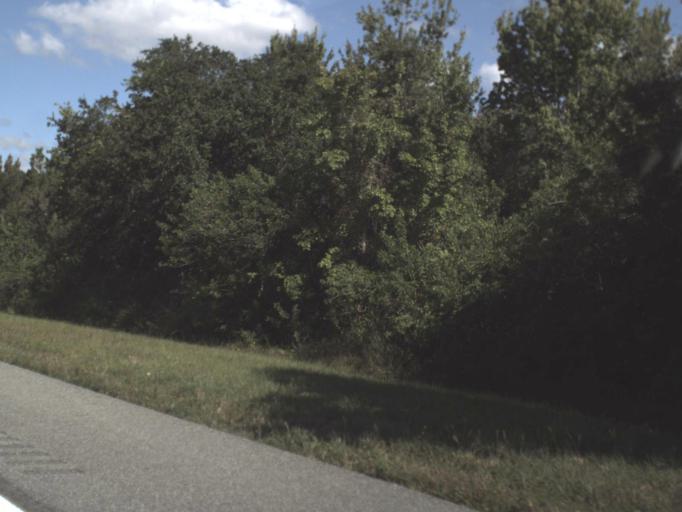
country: US
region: Florida
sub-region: Osceola County
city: Saint Cloud
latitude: 28.2104
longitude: -81.3079
